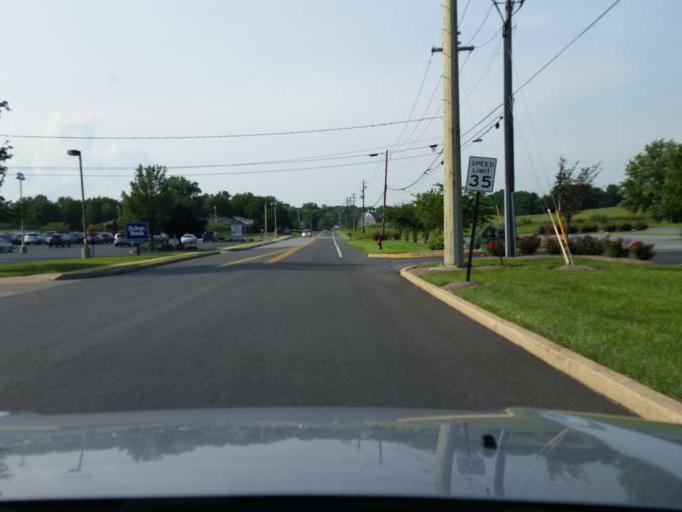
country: US
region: Pennsylvania
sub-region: Dauphin County
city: Hershey
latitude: 40.2694
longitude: -76.6479
